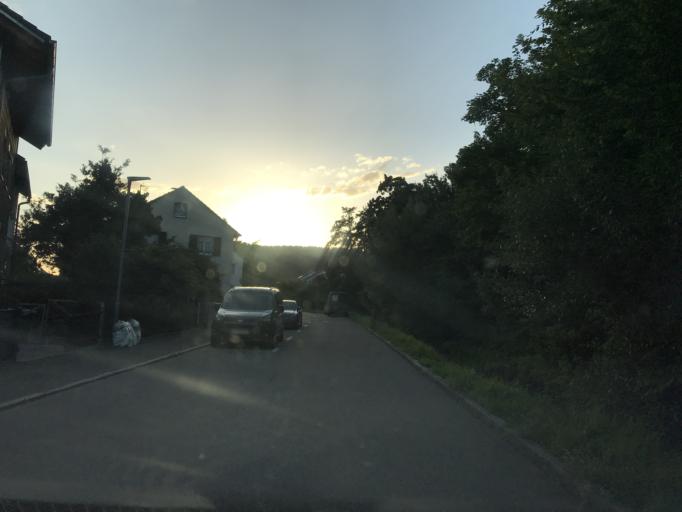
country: DE
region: Baden-Wuerttemberg
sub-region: Freiburg Region
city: Schopfheim
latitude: 47.6448
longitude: 7.8085
